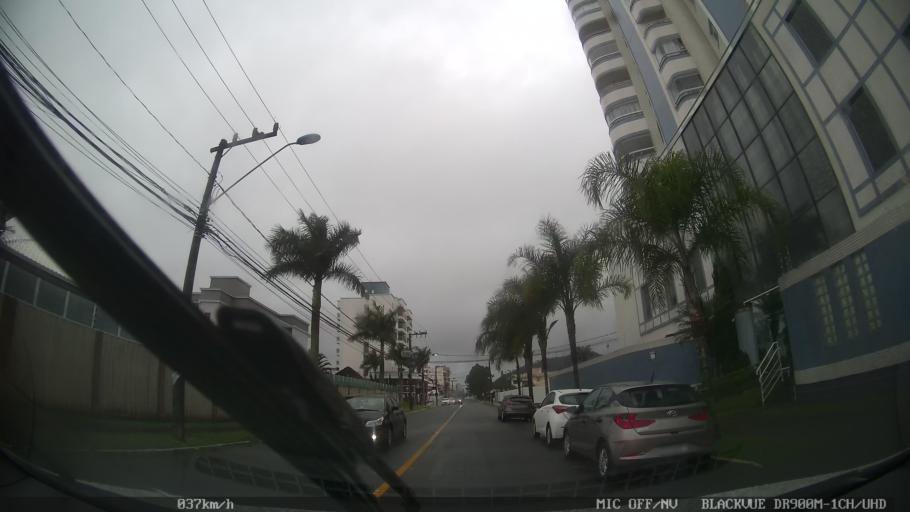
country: BR
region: Santa Catarina
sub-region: Itajai
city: Itajai
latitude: -26.9230
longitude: -48.6811
